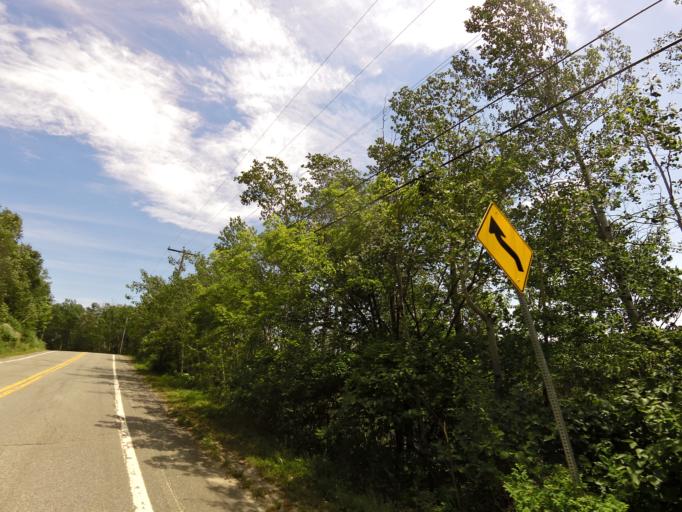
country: CA
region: Quebec
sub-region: Abitibi-Temiscamingue
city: Ville-Marie
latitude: 47.2914
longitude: -79.4470
